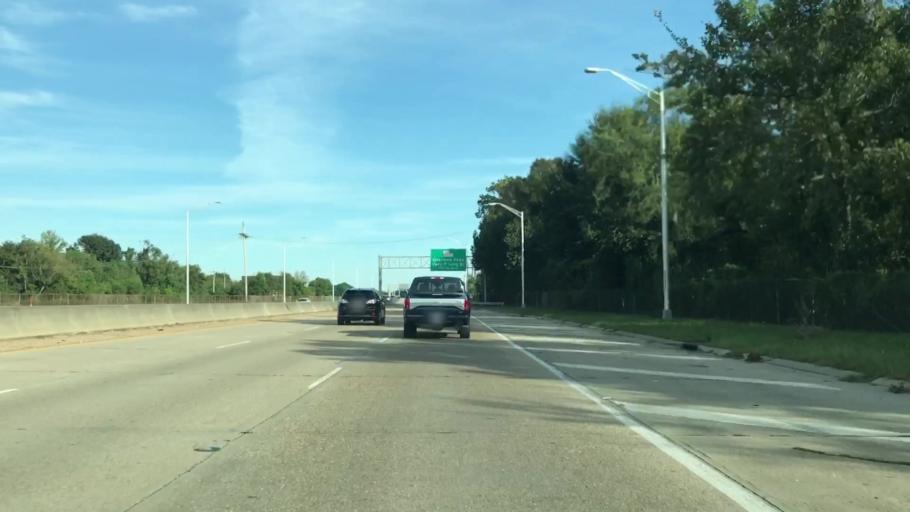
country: US
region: Louisiana
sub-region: Jefferson Parish
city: Elmwood
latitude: 29.9690
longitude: -90.1955
